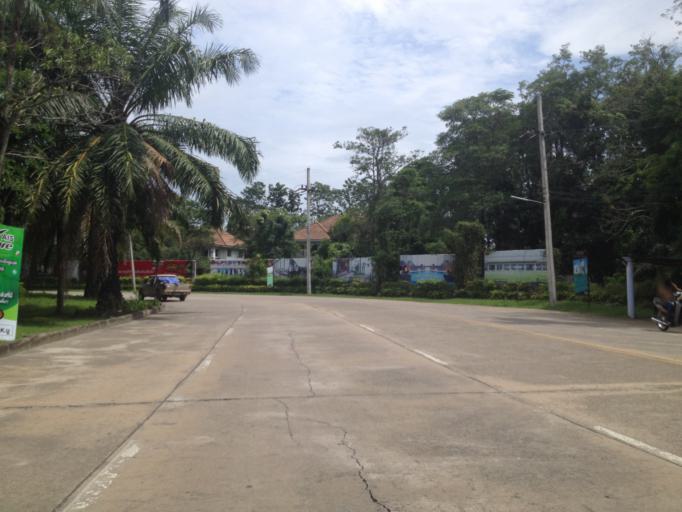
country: TH
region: Chiang Mai
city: Hang Dong
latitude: 18.7039
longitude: 98.9363
